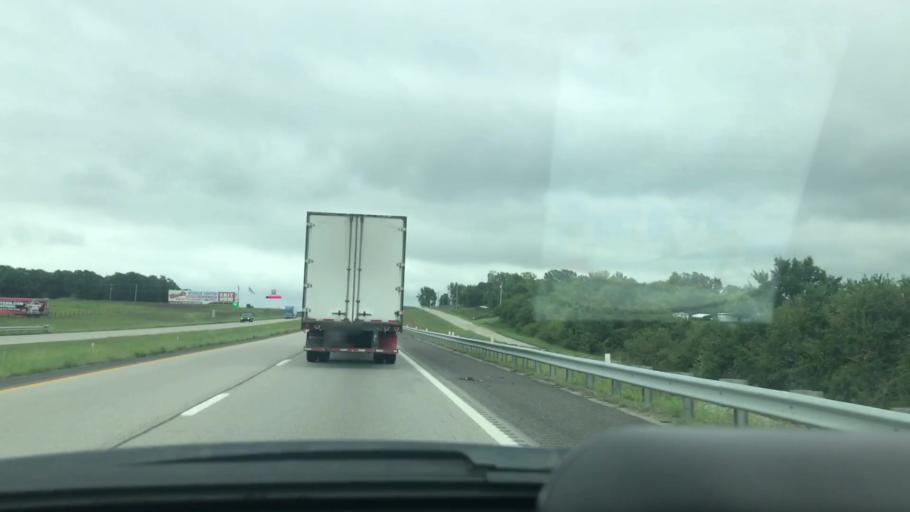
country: US
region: Missouri
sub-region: Greene County
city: Republic
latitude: 37.1842
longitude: -93.5797
